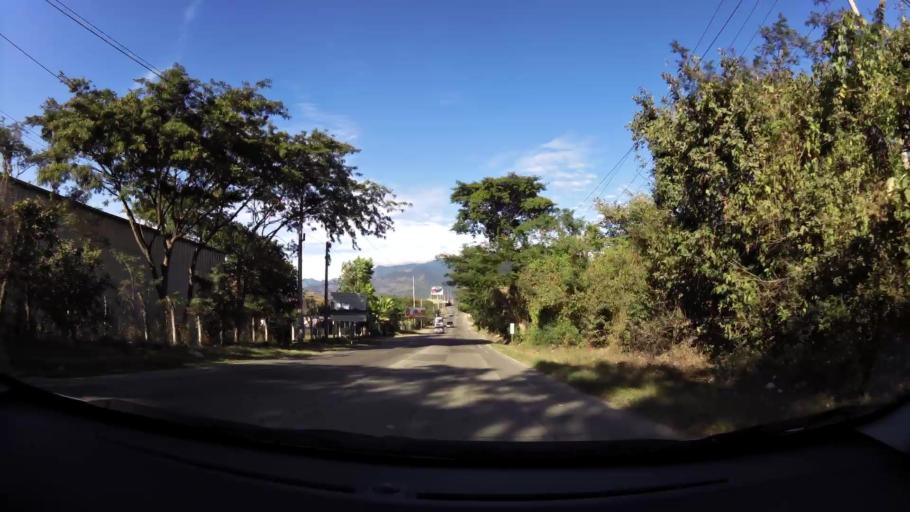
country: SV
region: Santa Ana
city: Metapan
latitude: 14.3120
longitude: -89.4507
